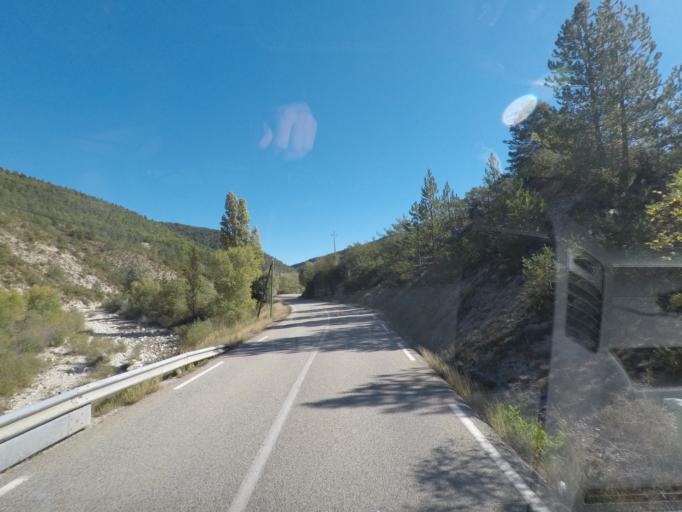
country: FR
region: Rhone-Alpes
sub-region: Departement de la Drome
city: Buis-les-Baronnies
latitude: 44.3895
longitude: 5.3854
